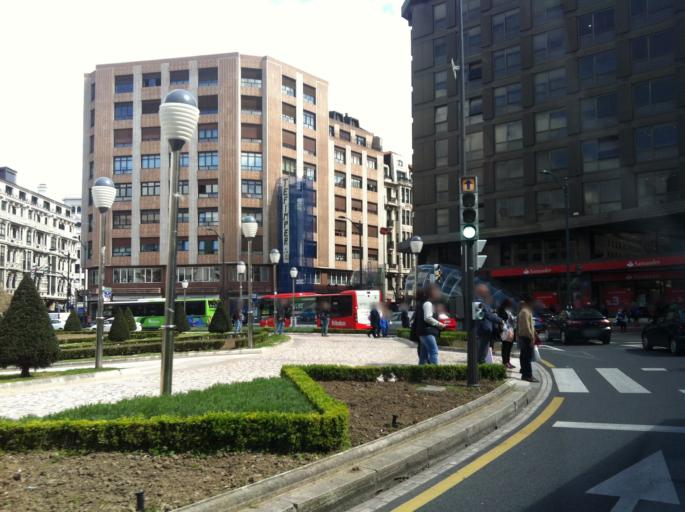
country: ES
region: Basque Country
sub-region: Bizkaia
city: Bilbao
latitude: 43.2628
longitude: -2.9346
